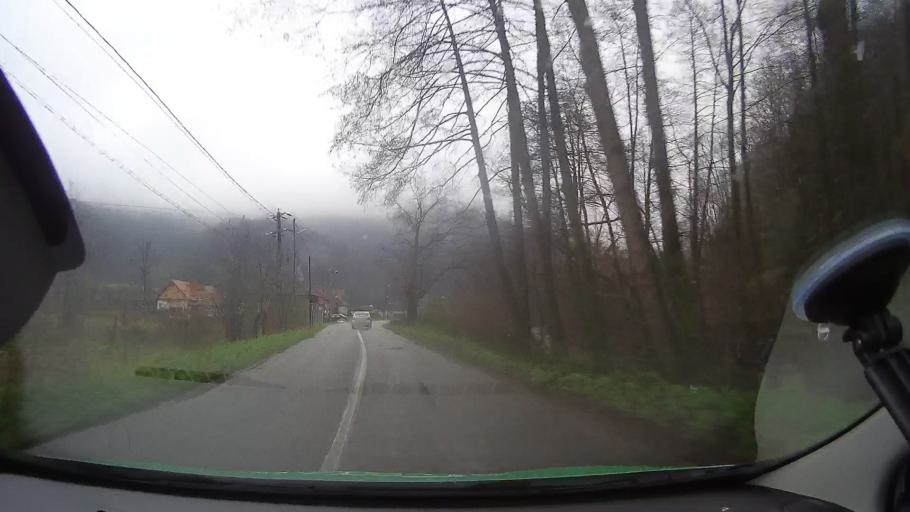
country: RO
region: Arad
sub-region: Comuna Dezna
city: Dezna
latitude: 46.4193
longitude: 22.2575
